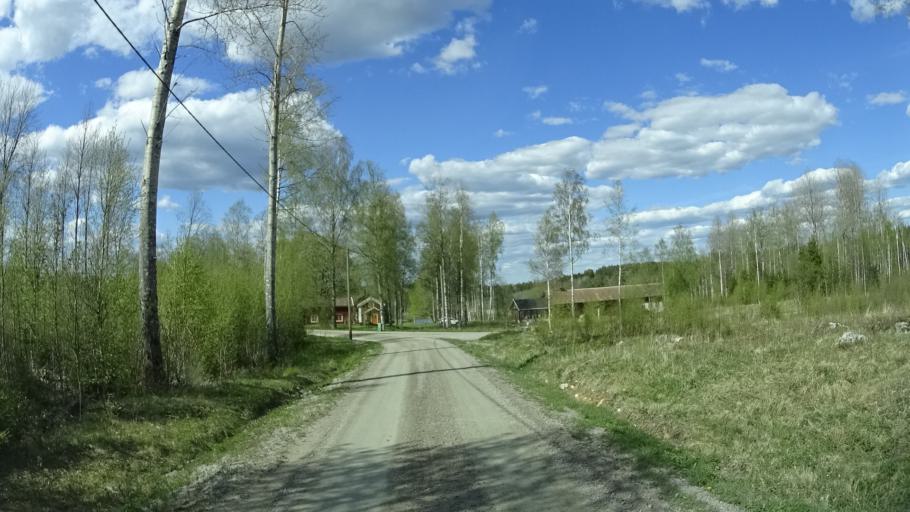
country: SE
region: OErebro
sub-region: Orebro Kommun
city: Garphyttan
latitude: 59.4252
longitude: 14.8662
